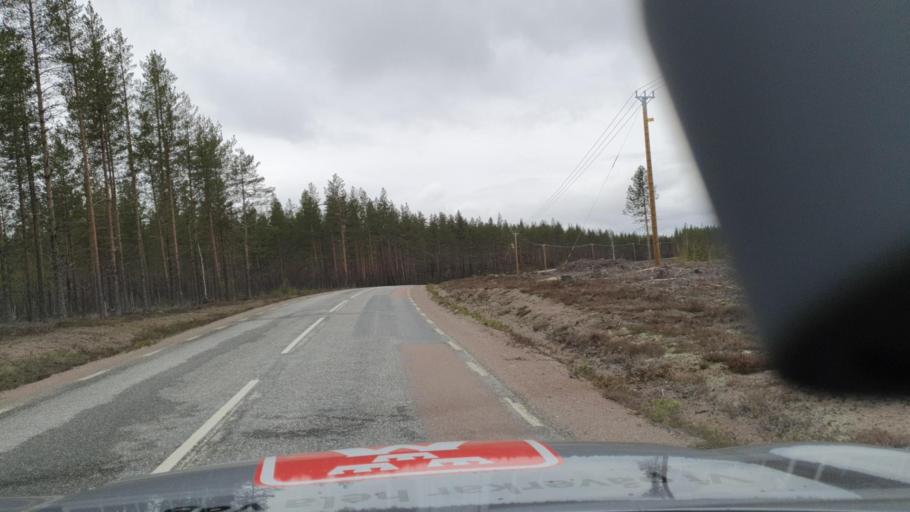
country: SE
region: Vaesternorrland
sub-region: Solleftea Kommun
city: Solleftea
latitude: 63.6128
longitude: 17.5105
